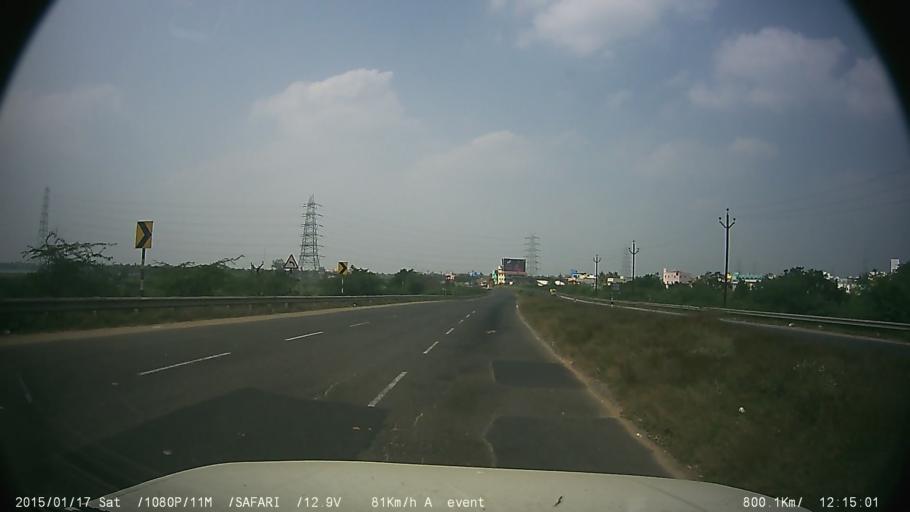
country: IN
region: Tamil Nadu
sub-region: Kancheepuram
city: Sriperumbudur
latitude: 12.9210
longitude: 79.8791
